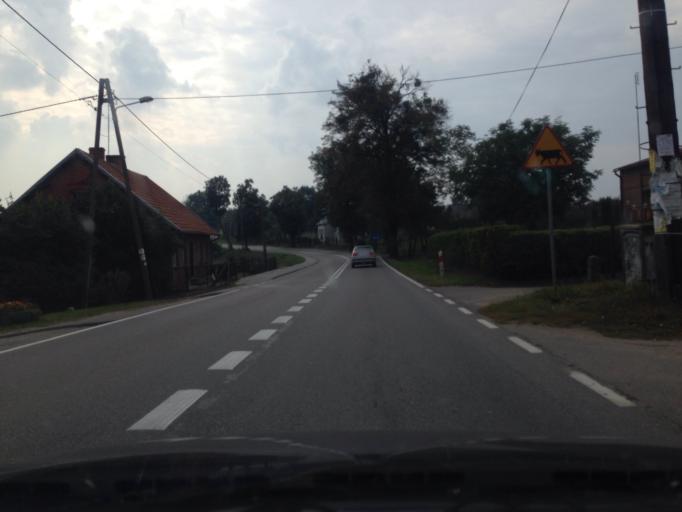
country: PL
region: Pomeranian Voivodeship
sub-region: Powiat kwidzynski
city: Ryjewo
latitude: 53.8732
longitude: 19.0016
